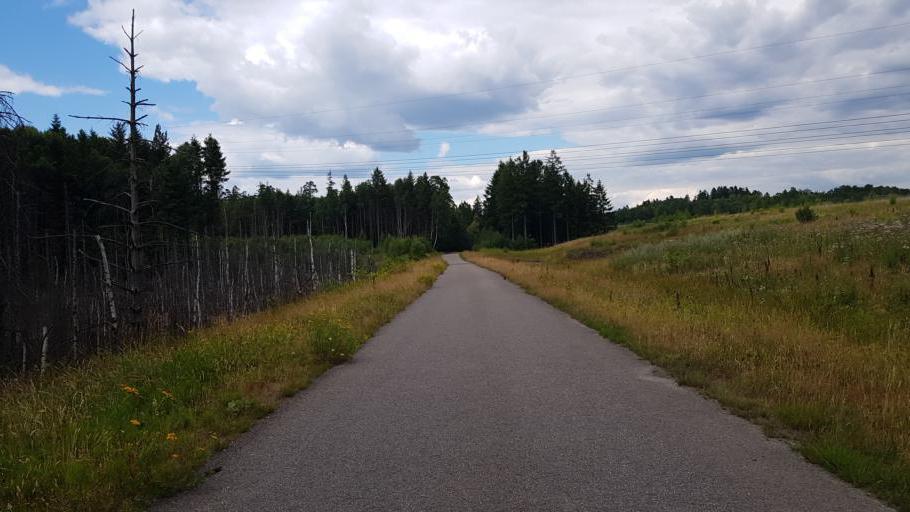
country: SE
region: Vaestra Goetaland
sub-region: Harryda Kommun
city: Molnlycke
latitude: 57.6781
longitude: 12.0861
